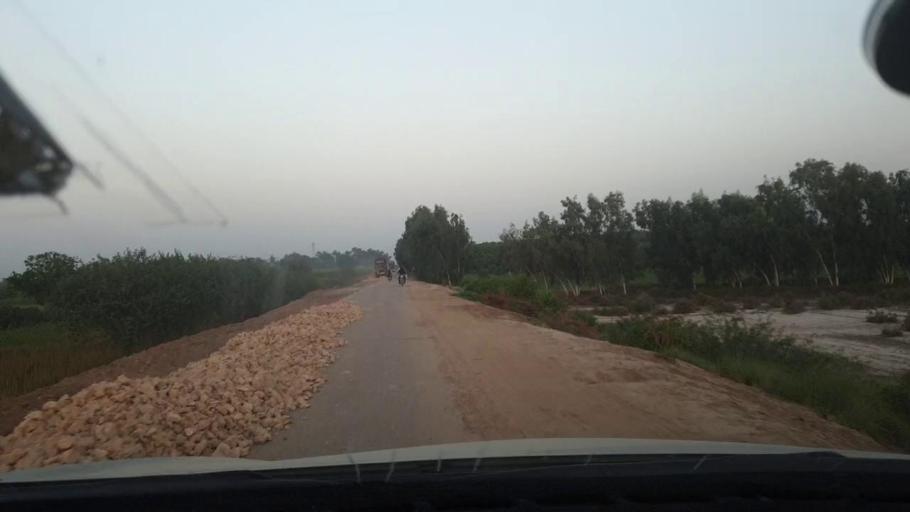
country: PK
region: Sindh
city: Bhit Shah
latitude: 25.7529
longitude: 68.5520
